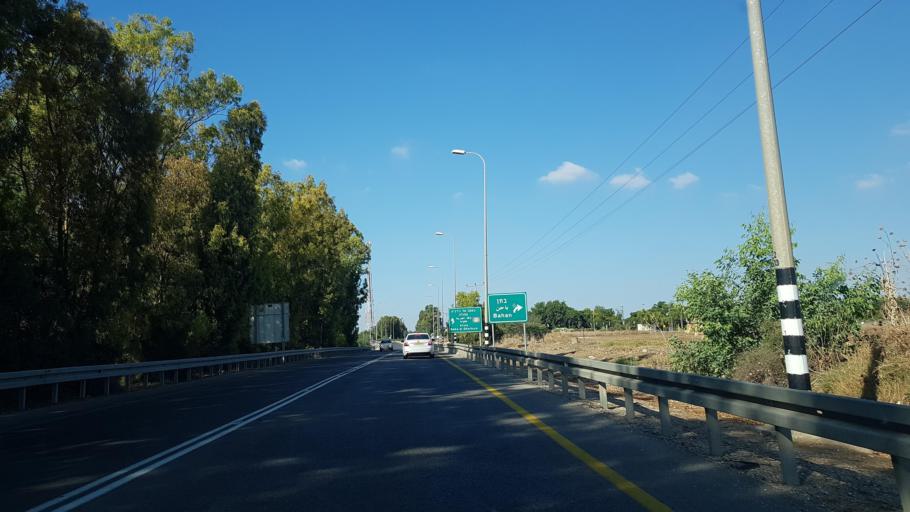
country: PS
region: West Bank
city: Tulkarm
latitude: 32.3481
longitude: 35.0127
